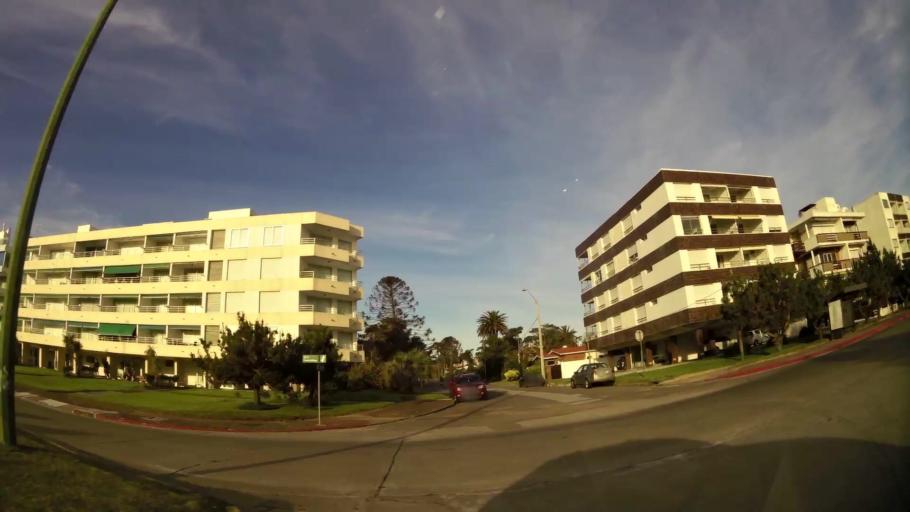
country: UY
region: Maldonado
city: Punta del Este
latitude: -34.9415
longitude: -54.9464
